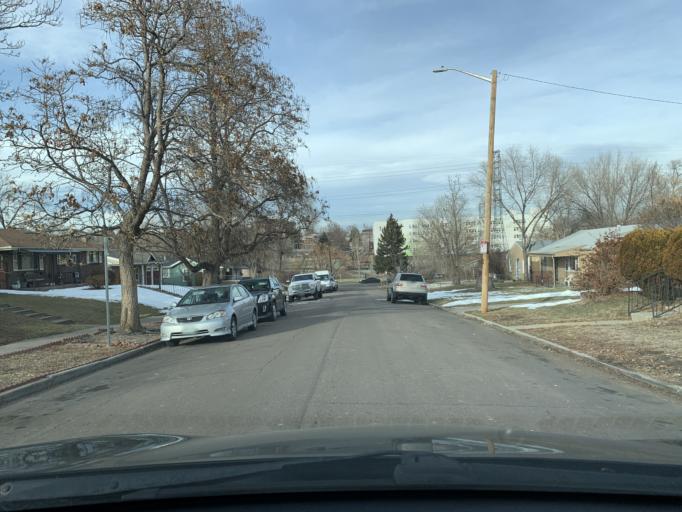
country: US
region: Colorado
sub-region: Jefferson County
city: Edgewater
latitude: 39.7338
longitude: -105.0333
